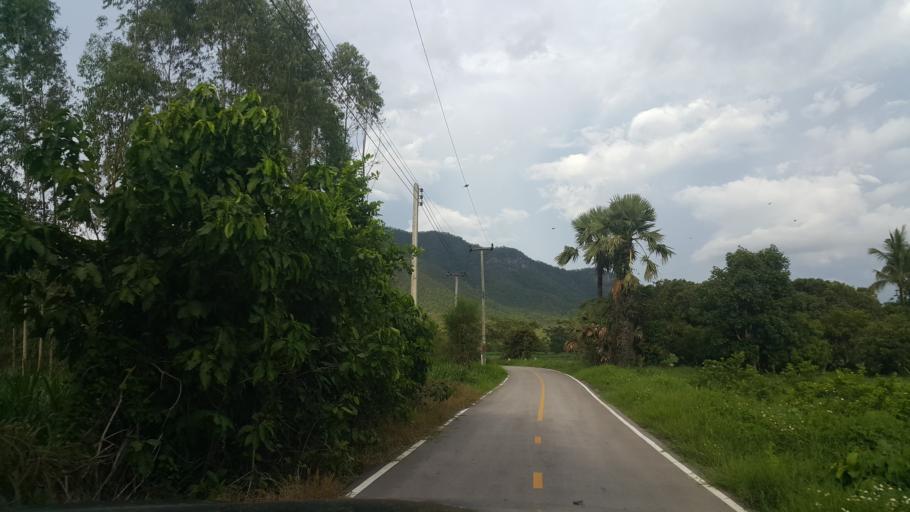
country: TH
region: Chiang Mai
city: Mae On
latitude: 18.7231
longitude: 99.2245
